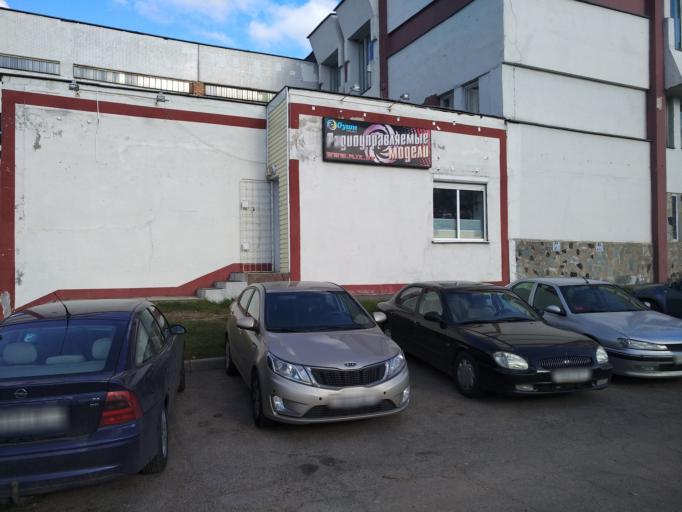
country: BY
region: Minsk
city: Minsk
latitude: 53.9369
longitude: 27.5795
